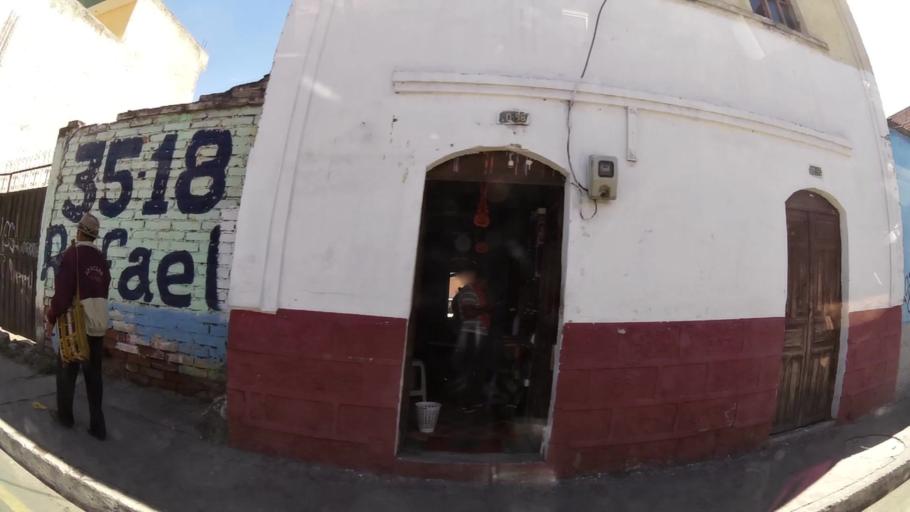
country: EC
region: Chimborazo
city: Riobamba
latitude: -1.6791
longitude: -78.6427
